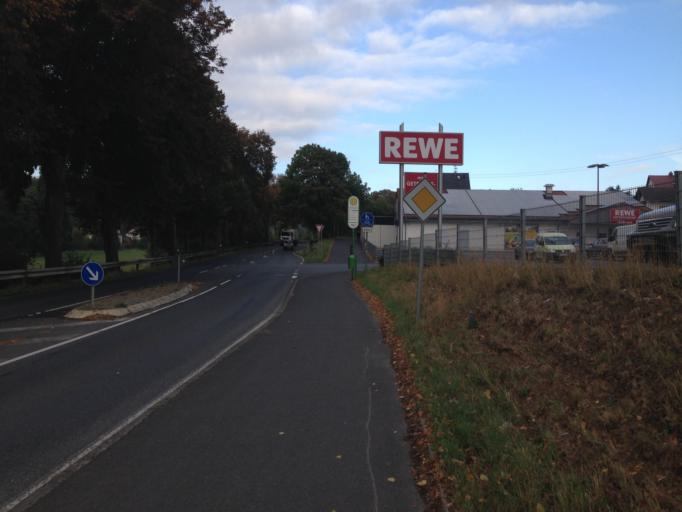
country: DE
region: Hesse
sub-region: Regierungsbezirk Giessen
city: Heuchelheim
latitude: 50.6132
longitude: 8.6095
